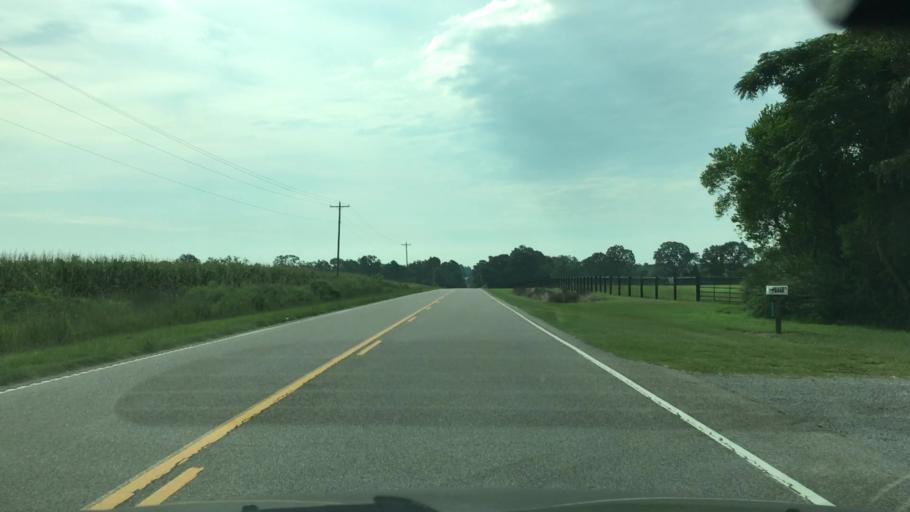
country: US
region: South Carolina
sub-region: Lexington County
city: Batesburg-Leesville
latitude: 33.6896
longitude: -81.4686
